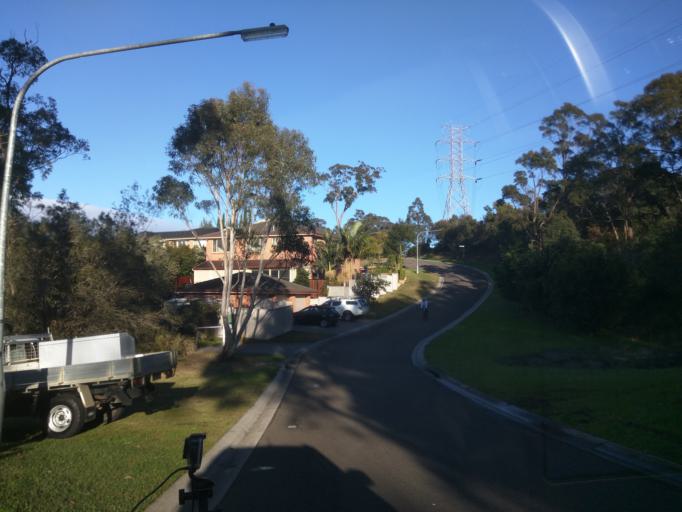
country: AU
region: New South Wales
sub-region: Sutherland Shire
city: Menai
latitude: -34.0226
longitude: 151.0244
